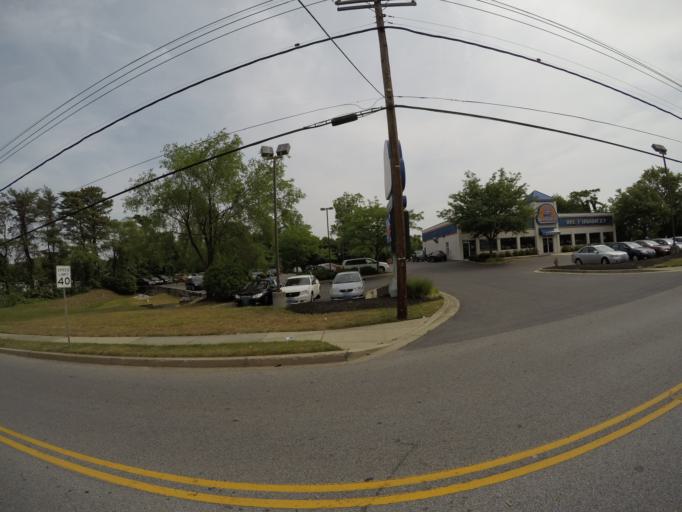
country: US
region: Maryland
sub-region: Anne Arundel County
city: Glen Burnie
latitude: 39.1766
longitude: -76.6194
